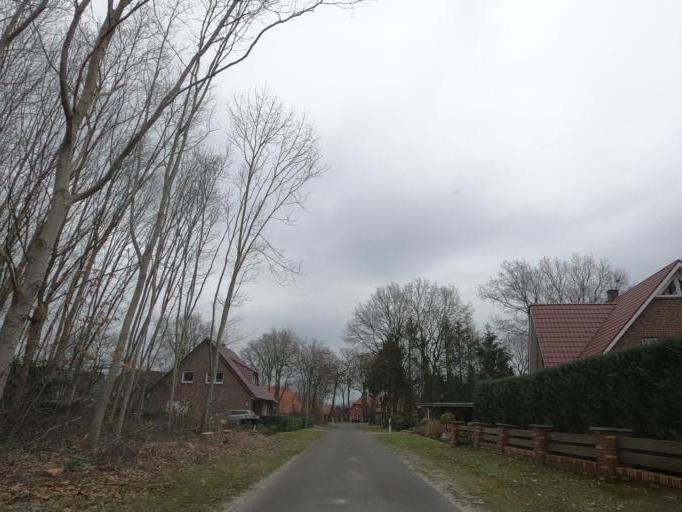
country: DE
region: Lower Saxony
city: Hilkenbrook
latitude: 52.9781
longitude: 7.7710
